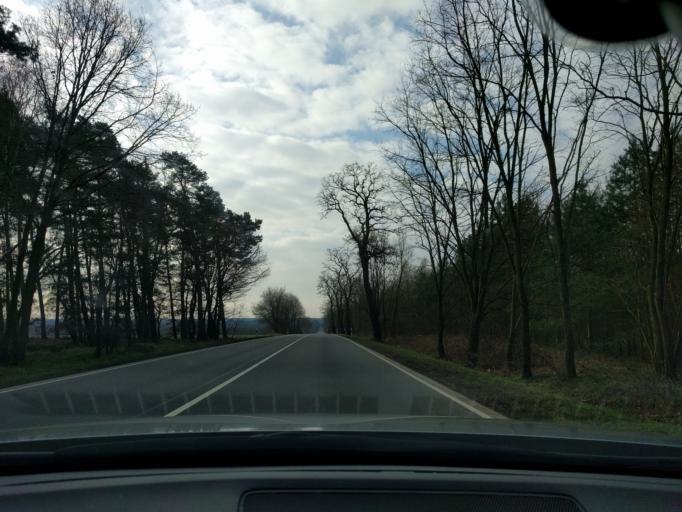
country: DE
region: Saxony-Anhalt
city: Colbitz
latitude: 52.3902
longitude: 11.6195
